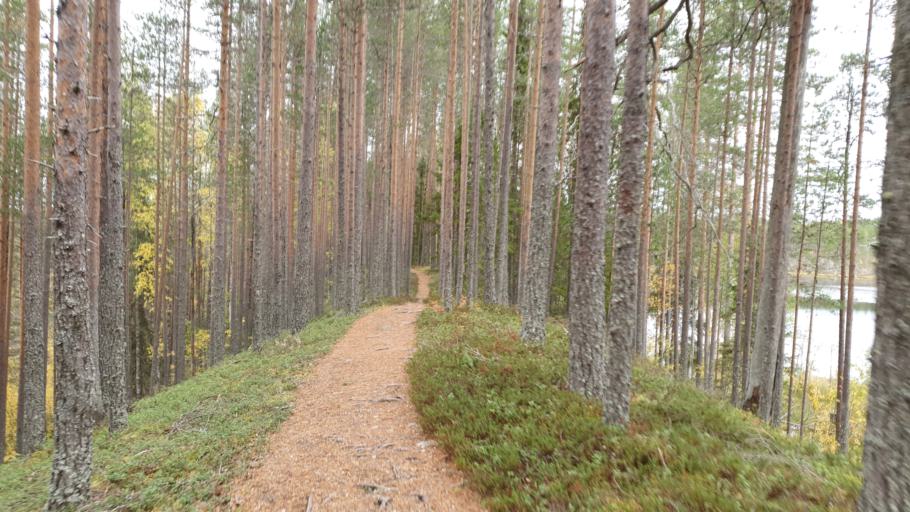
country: FI
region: Kainuu
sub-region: Kehys-Kainuu
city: Kuhmo
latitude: 64.2926
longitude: 29.3540
